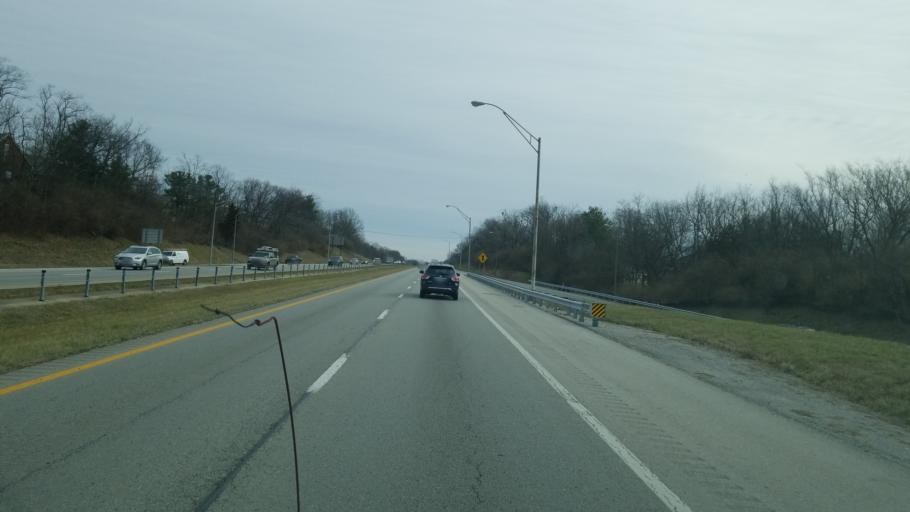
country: US
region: Kentucky
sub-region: Fayette County
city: Lexington
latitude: 37.9911
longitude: -84.4930
